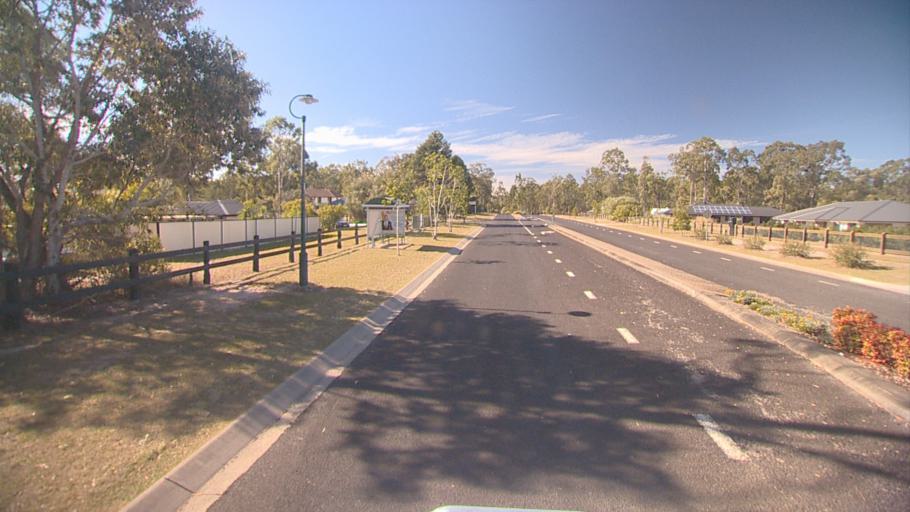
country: AU
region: Queensland
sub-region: Ipswich
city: Springfield Lakes
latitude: -27.7352
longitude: 152.9204
